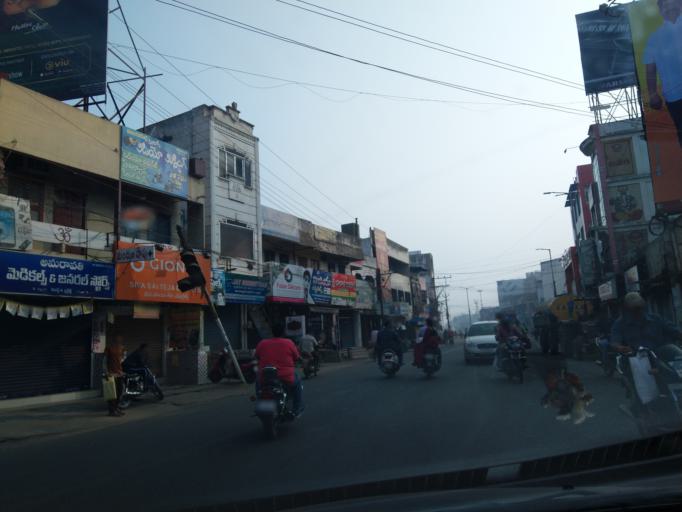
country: IN
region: Andhra Pradesh
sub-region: West Godavari
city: Bhimavaram
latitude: 16.5448
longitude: 81.5206
